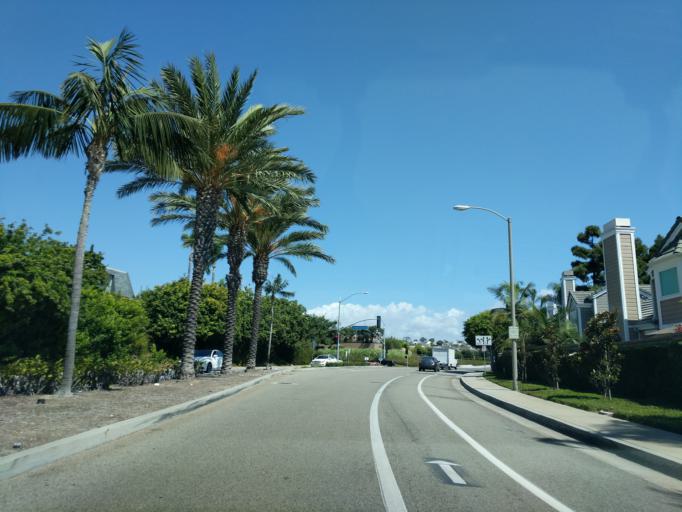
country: US
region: California
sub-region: Orange County
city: Dana Point
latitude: 33.4701
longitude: -117.7139
